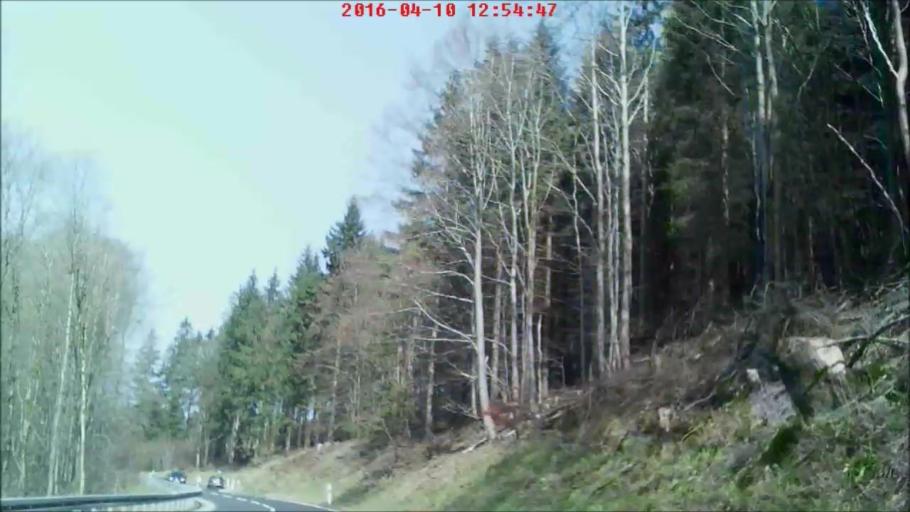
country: DE
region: Thuringia
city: Pappenheim
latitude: 50.8207
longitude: 10.5203
